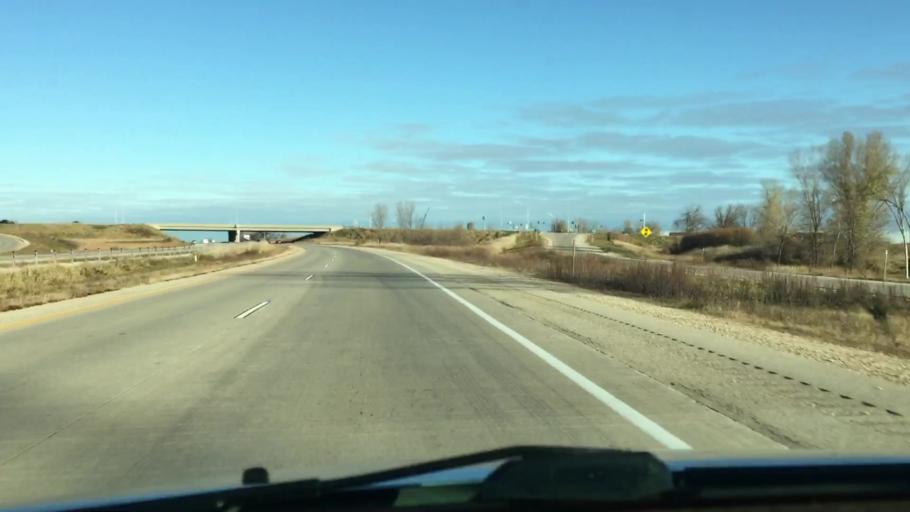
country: US
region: Wisconsin
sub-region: Fond du Lac County
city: Fond du Lac
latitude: 43.7340
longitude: -88.4426
